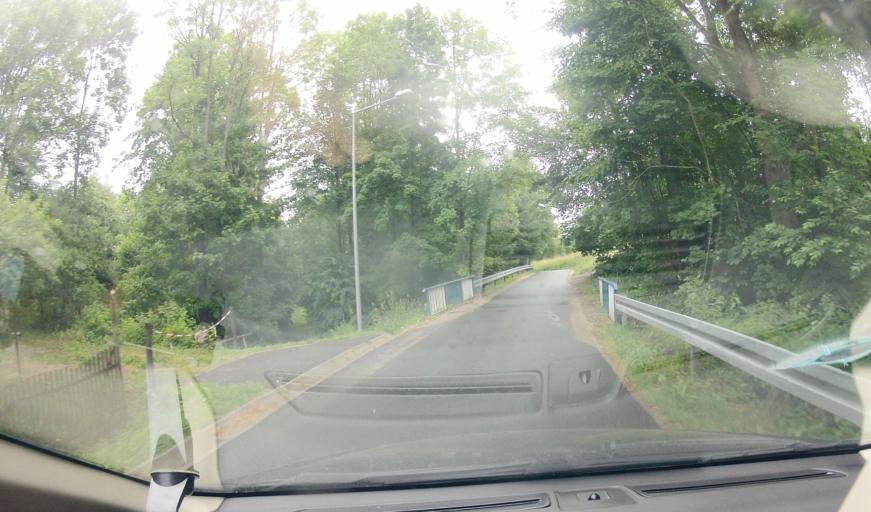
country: PL
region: Lower Silesian Voivodeship
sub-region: Powiat klodzki
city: Miedzylesie
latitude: 50.1190
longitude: 16.6449
